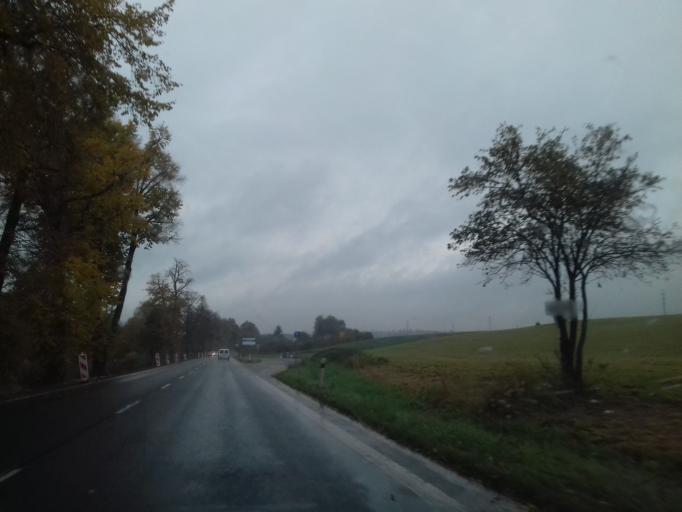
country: CZ
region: Liberecky
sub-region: Okres Semily
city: Turnov
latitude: 50.5647
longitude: 15.1909
